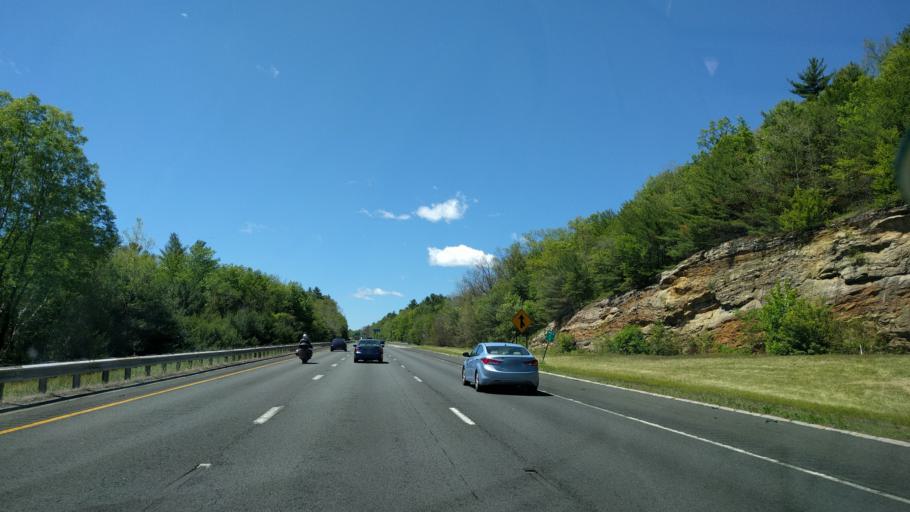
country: US
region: Massachusetts
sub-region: Worcester County
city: Sturbridge
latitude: 42.0912
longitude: -72.0912
